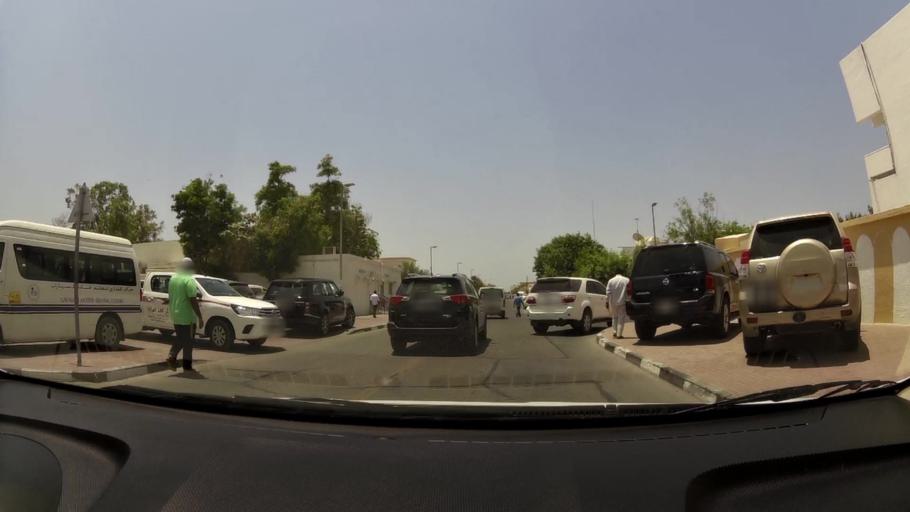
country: AE
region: Ash Shariqah
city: Sharjah
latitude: 25.2896
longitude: 55.3332
